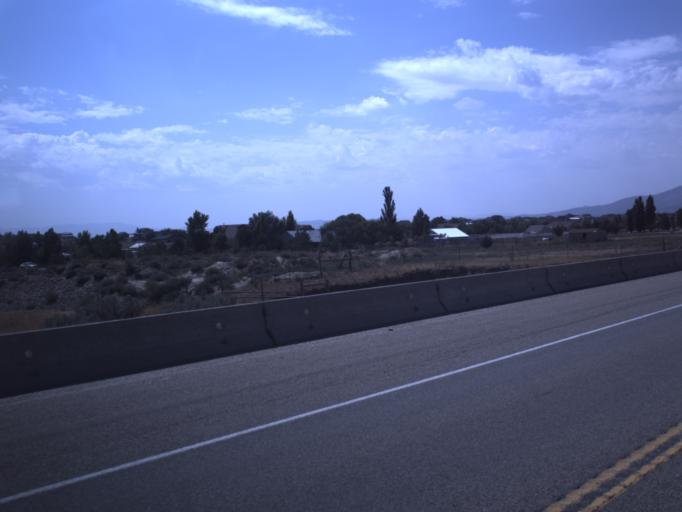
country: US
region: Utah
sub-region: Utah County
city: Eagle Mountain
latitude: 40.3775
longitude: -112.0043
